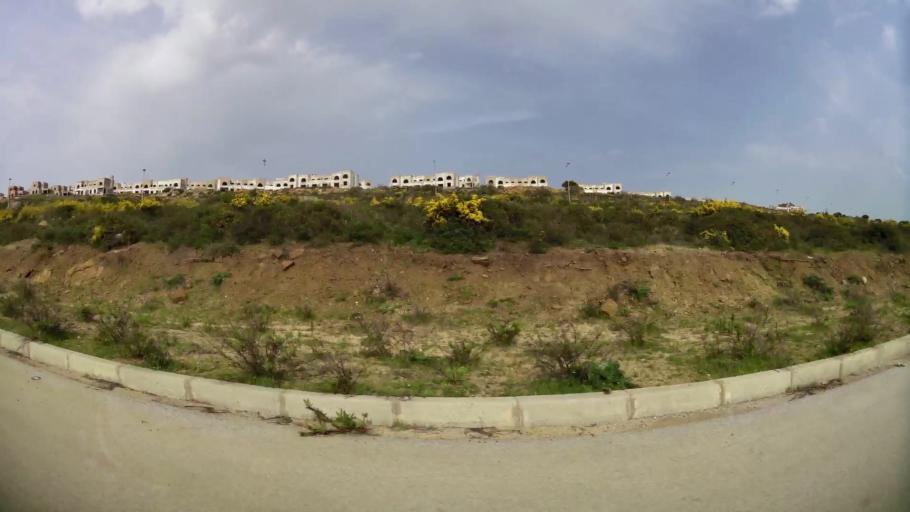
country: MA
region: Tanger-Tetouan
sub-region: Tanger-Assilah
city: Boukhalef
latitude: 35.6950
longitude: -5.9407
